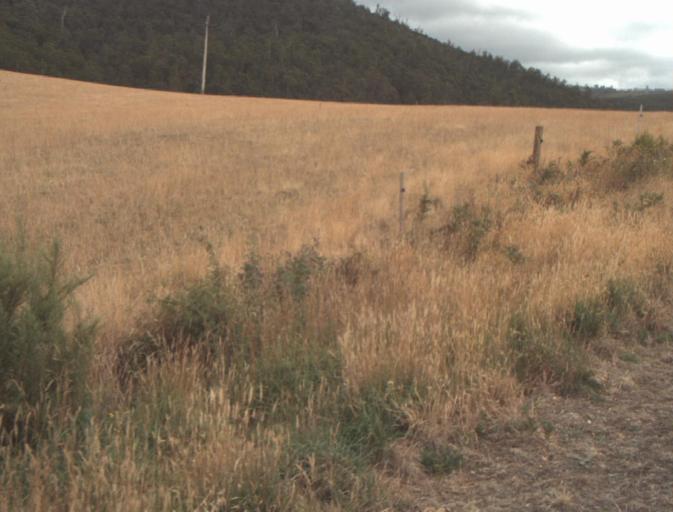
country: AU
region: Tasmania
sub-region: Northern Midlands
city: Evandale
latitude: -41.4727
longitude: 147.4971
